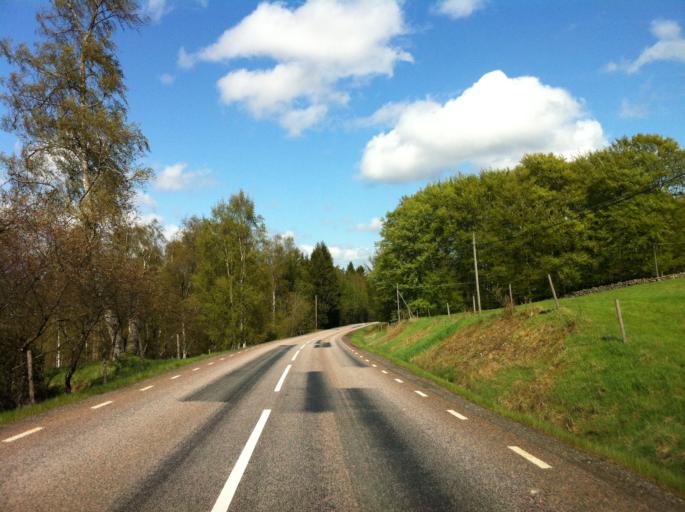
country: SE
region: Vaestra Goetaland
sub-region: Alingsas Kommun
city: Ingared
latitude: 57.8457
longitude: 12.5185
